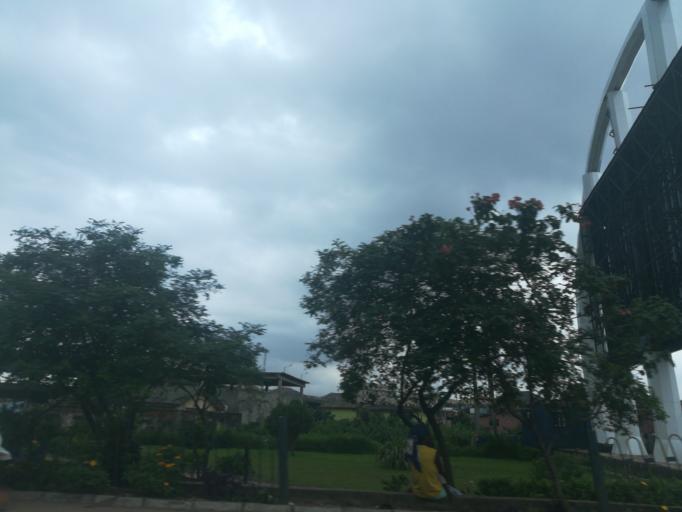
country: NG
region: Lagos
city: Somolu
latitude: 6.5476
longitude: 3.3972
